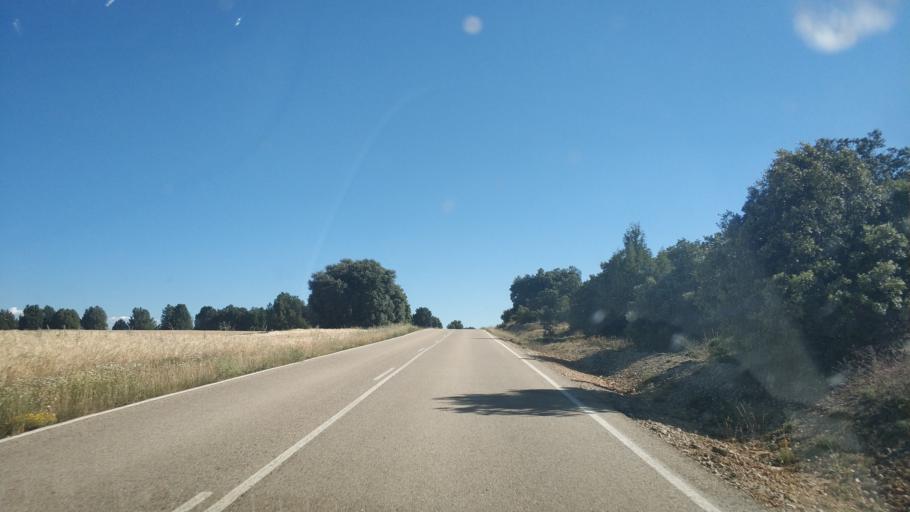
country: ES
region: Castille and Leon
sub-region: Provincia de Soria
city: Liceras
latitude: 41.4553
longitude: -3.2119
